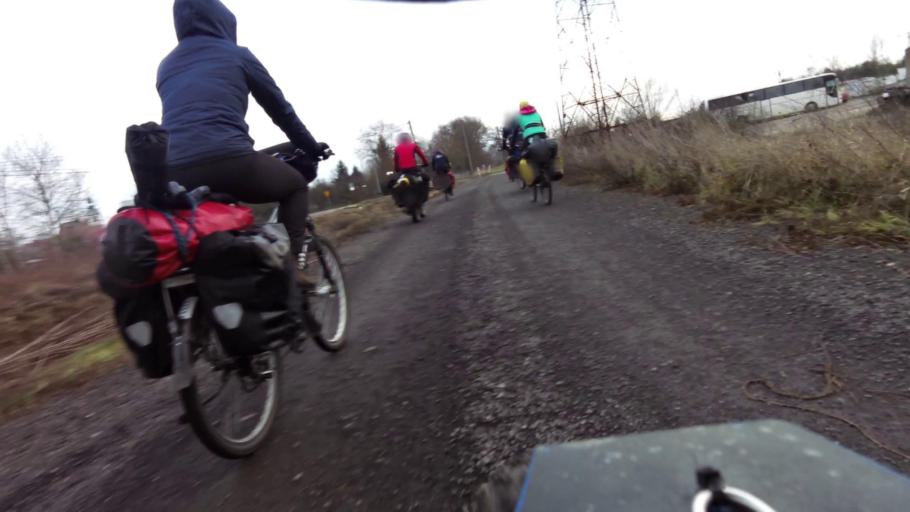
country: PL
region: Lubusz
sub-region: Powiat gorzowski
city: Jenin
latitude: 52.7079
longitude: 15.1319
